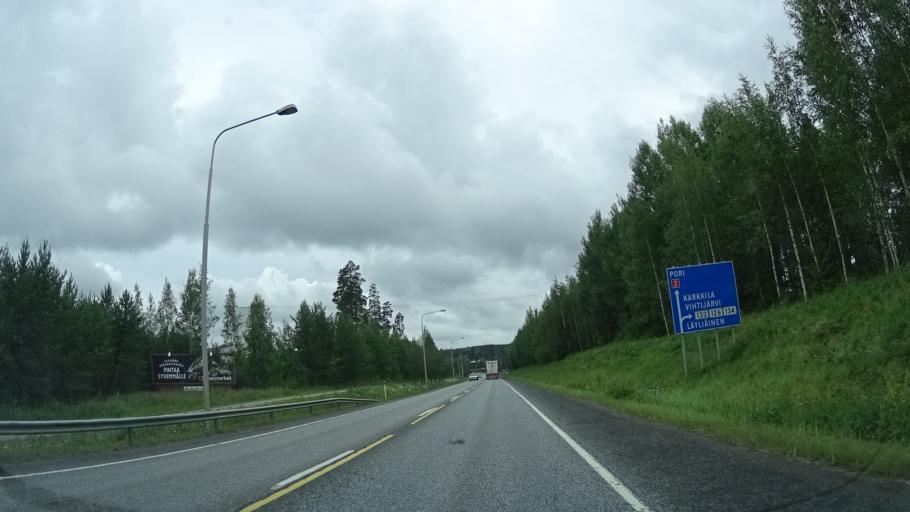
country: FI
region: Uusimaa
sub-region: Helsinki
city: Karkkila
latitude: 60.5277
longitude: 24.2391
